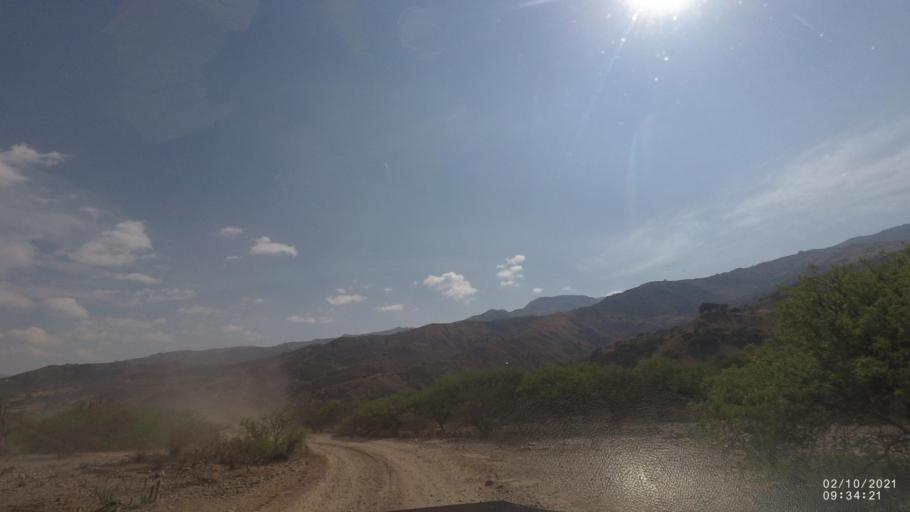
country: BO
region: Cochabamba
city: Irpa Irpa
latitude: -17.8399
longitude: -66.3193
